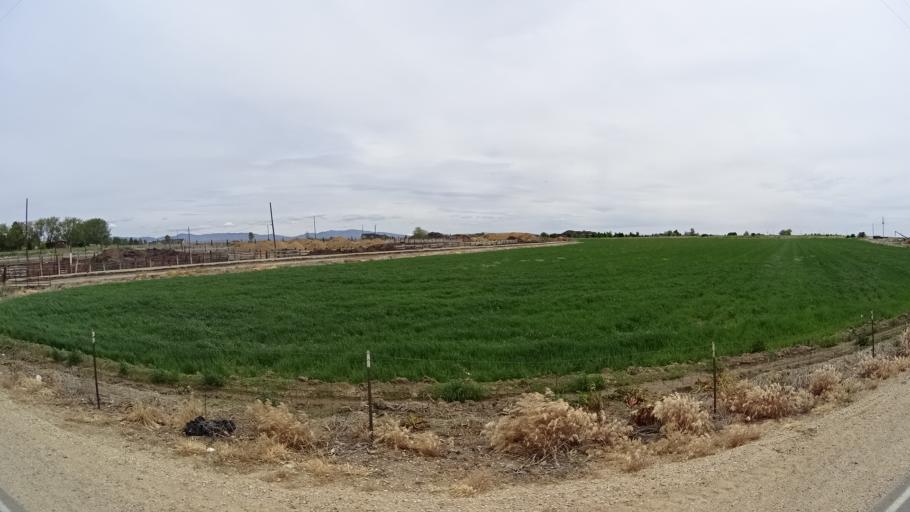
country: US
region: Idaho
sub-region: Ada County
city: Meridian
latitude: 43.5520
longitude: -116.3749
